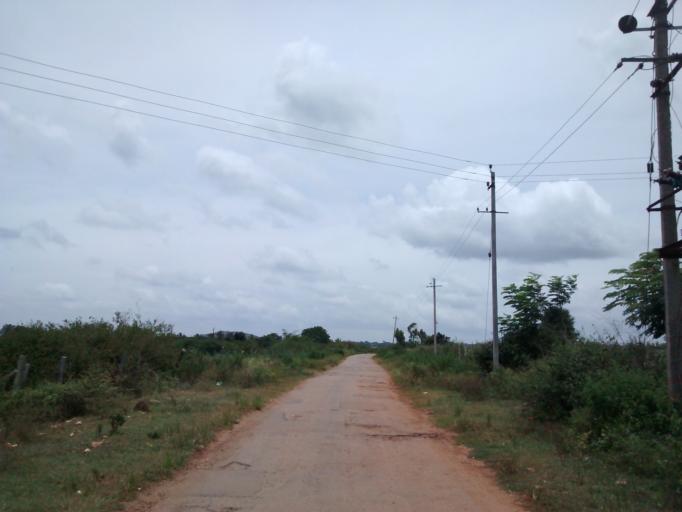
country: IN
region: Karnataka
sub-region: Hassan
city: Hassan
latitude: 12.9205
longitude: 76.1311
